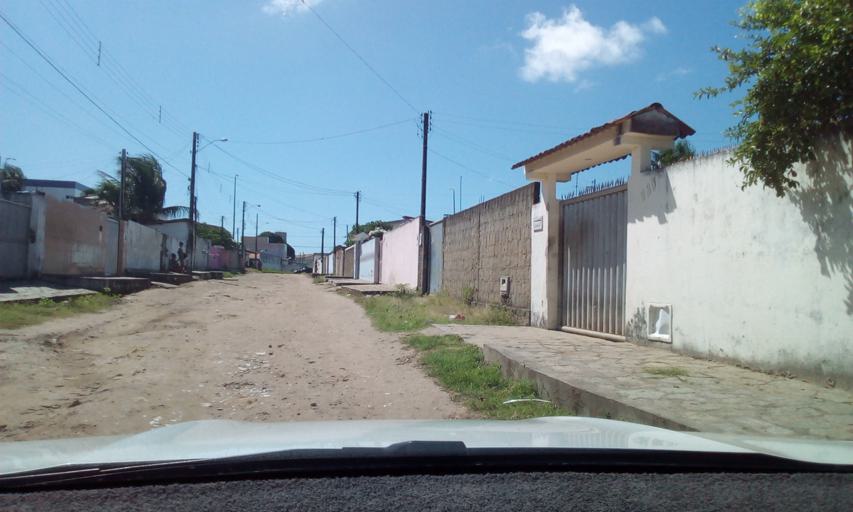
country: BR
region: Paraiba
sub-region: Joao Pessoa
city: Joao Pessoa
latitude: -7.2020
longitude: -34.8342
